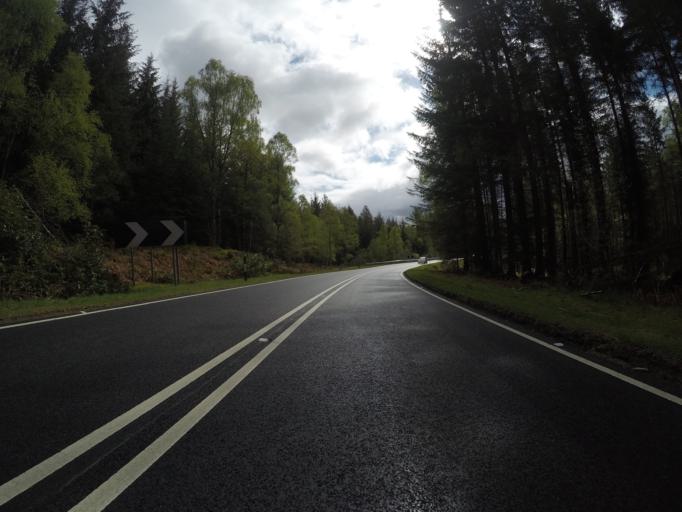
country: GB
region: Scotland
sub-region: Highland
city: Spean Bridge
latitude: 57.0749
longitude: -4.8361
